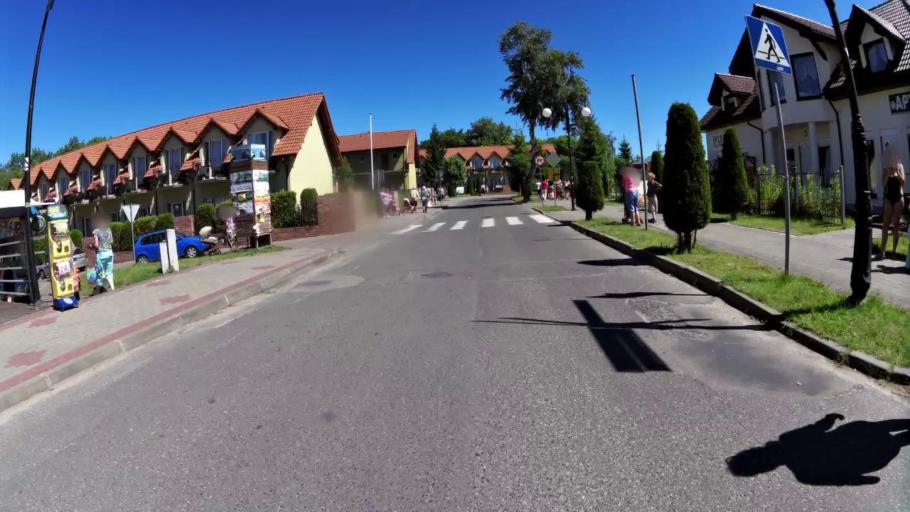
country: PL
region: West Pomeranian Voivodeship
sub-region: Powiat gryficki
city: Rewal
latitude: 54.0837
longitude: 15.0214
